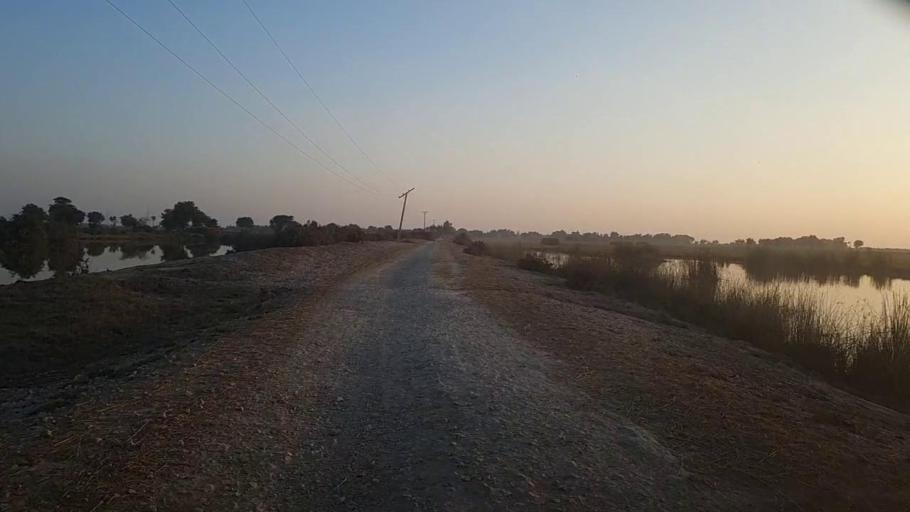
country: PK
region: Sindh
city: Khairpur Nathan Shah
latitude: 27.1642
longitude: 67.7322
